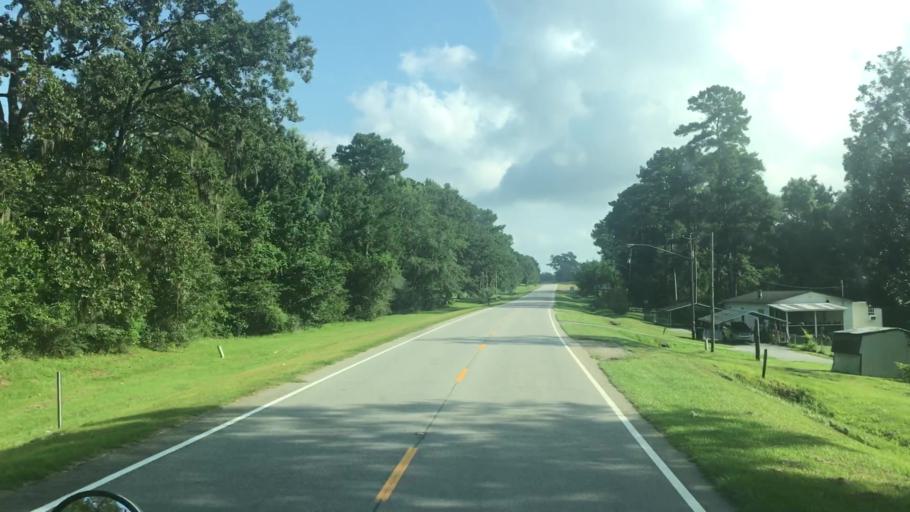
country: US
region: Florida
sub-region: Gadsden County
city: Havana
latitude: 30.7541
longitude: -84.4880
